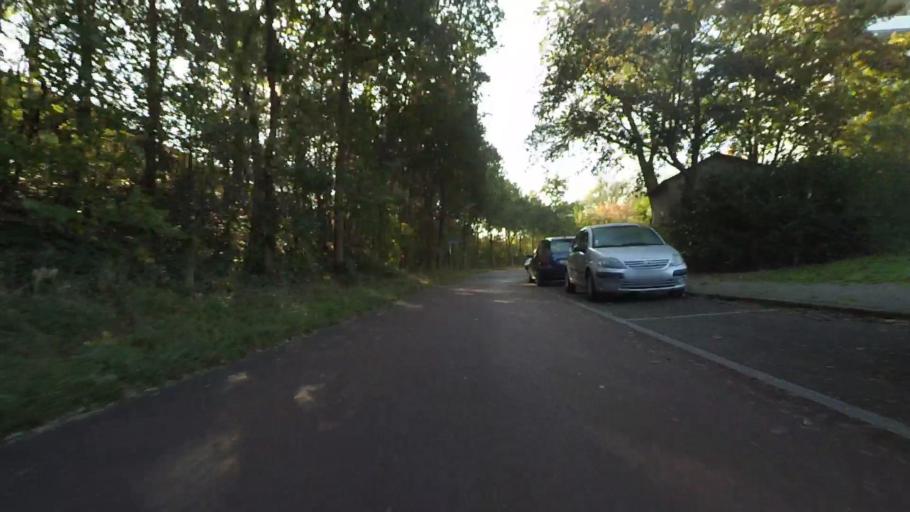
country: NL
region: Gelderland
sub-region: Gemeente Harderwijk
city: Harderwijk
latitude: 52.3385
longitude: 5.6444
